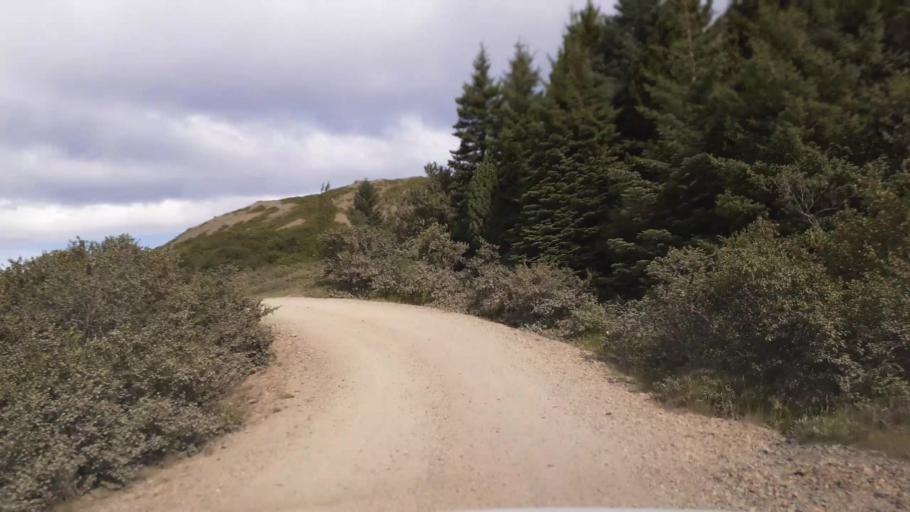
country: IS
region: East
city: Hoefn
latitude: 64.4386
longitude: -14.9138
